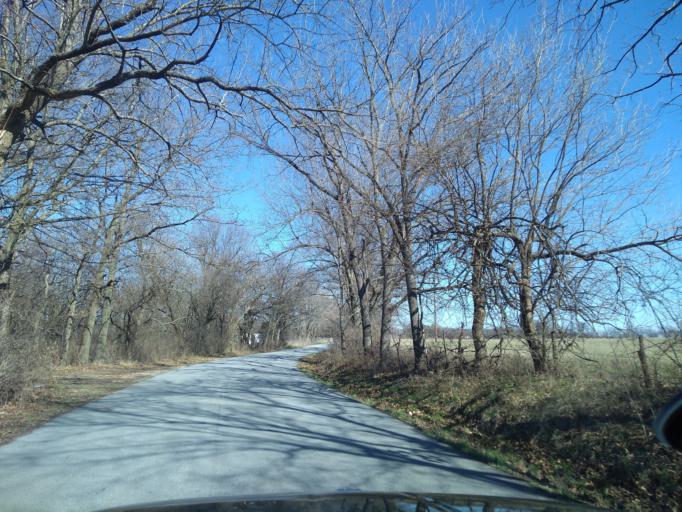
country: US
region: Arkansas
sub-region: Washington County
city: Farmington
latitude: 36.0609
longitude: -94.2502
